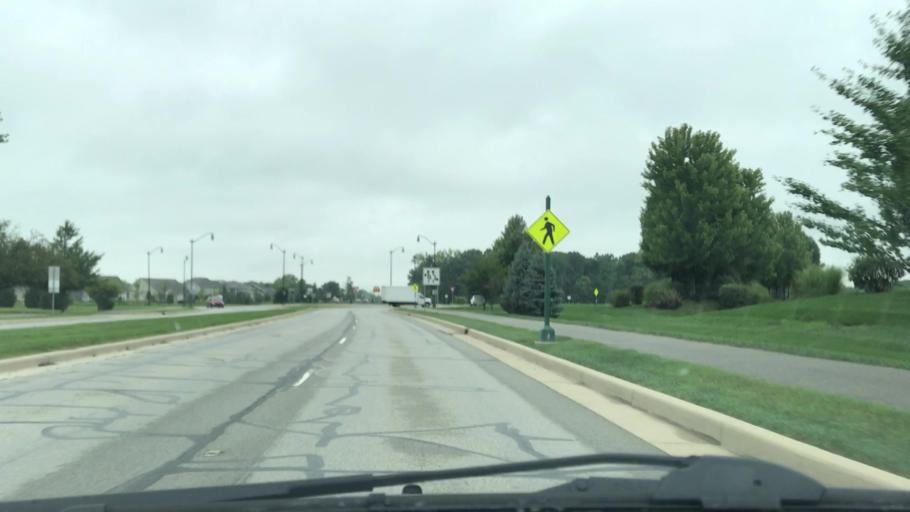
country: US
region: Indiana
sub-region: Hamilton County
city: Westfield
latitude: 40.0208
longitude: -86.0706
